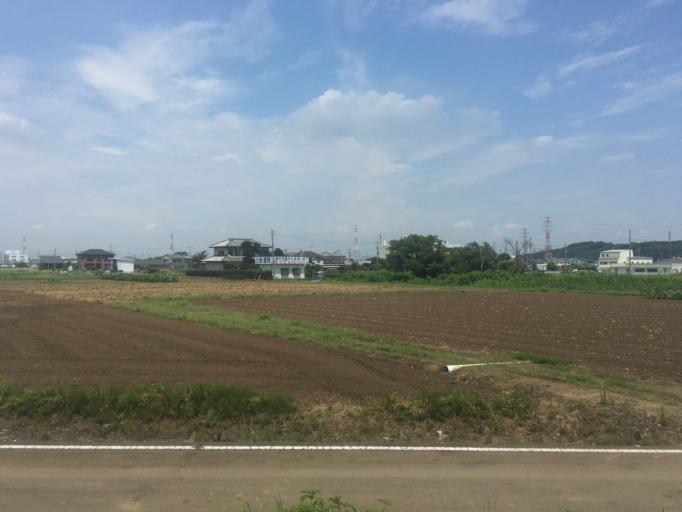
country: JP
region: Saitama
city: Kodamacho-kodamaminami
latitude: 36.1754
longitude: 139.1790
